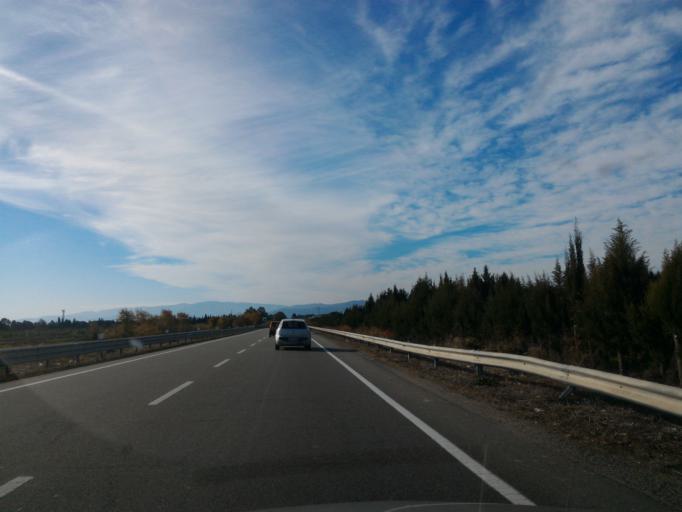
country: IT
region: Calabria
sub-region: Provincia di Catanzaro
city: Barone
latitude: 38.8655
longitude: 16.6840
